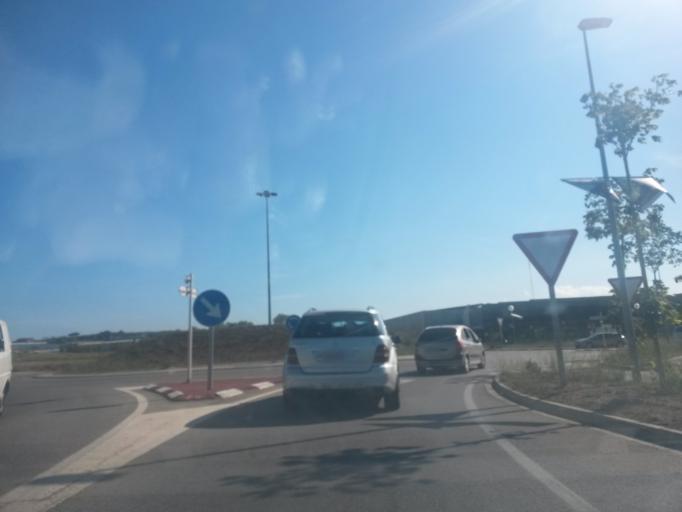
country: ES
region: Catalonia
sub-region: Provincia de Girona
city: Palafrugell
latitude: 41.9328
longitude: 3.1588
